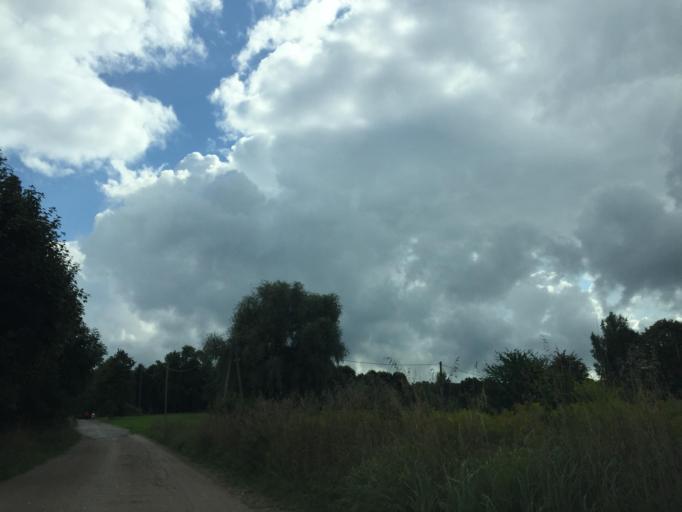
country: LV
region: Raunas
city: Rauna
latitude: 57.3380
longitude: 25.4857
